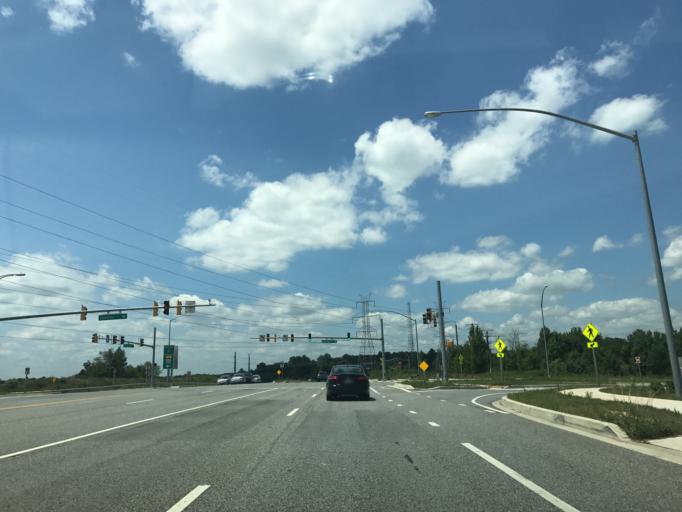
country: US
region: Maryland
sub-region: Prince George's County
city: West Laurel
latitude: 39.0863
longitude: -76.8996
